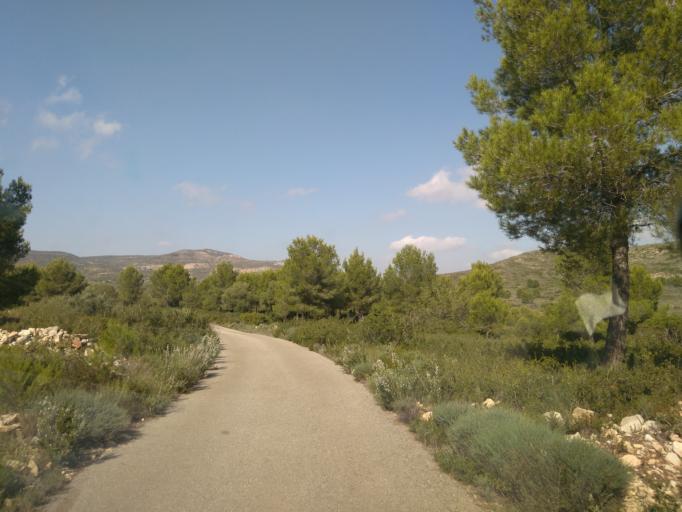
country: ES
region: Valencia
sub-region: Provincia de Valencia
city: Tous
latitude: 39.1802
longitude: -0.6302
